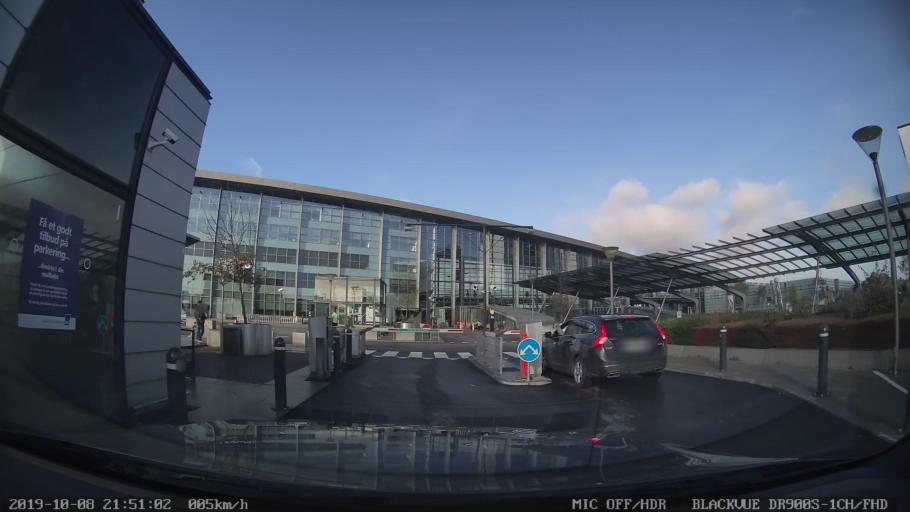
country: DK
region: Capital Region
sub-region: Dragor Kommune
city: Dragor
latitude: 55.6282
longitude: 12.6640
